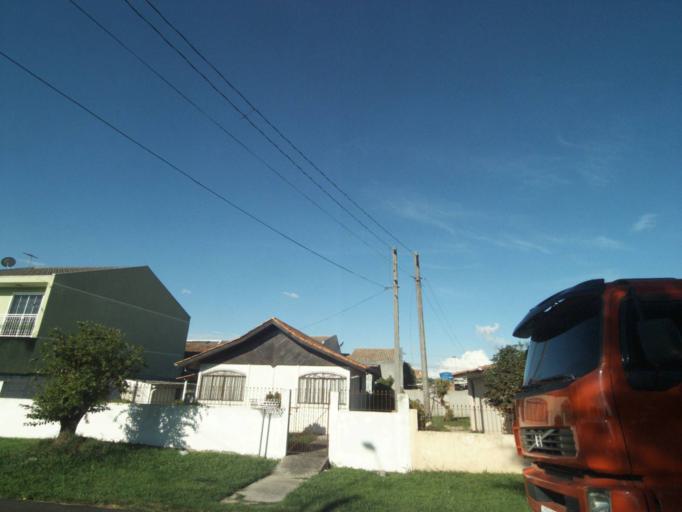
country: BR
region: Parana
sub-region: Pinhais
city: Pinhais
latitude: -25.4492
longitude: -49.2059
